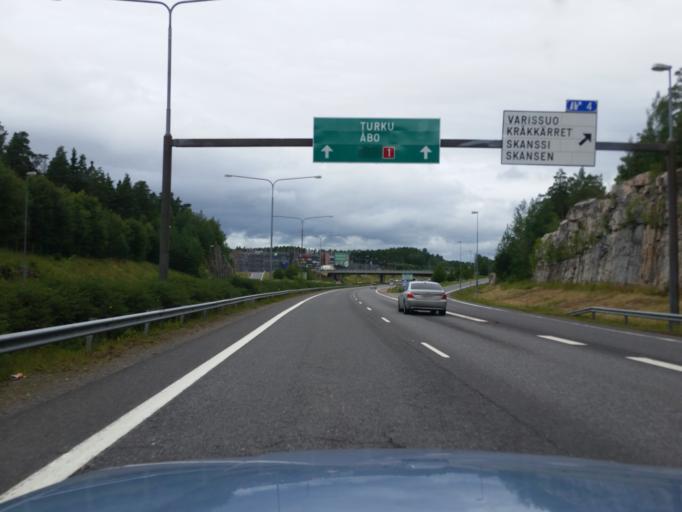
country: FI
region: Varsinais-Suomi
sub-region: Turku
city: Kaarina
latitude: 60.4264
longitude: 22.3318
